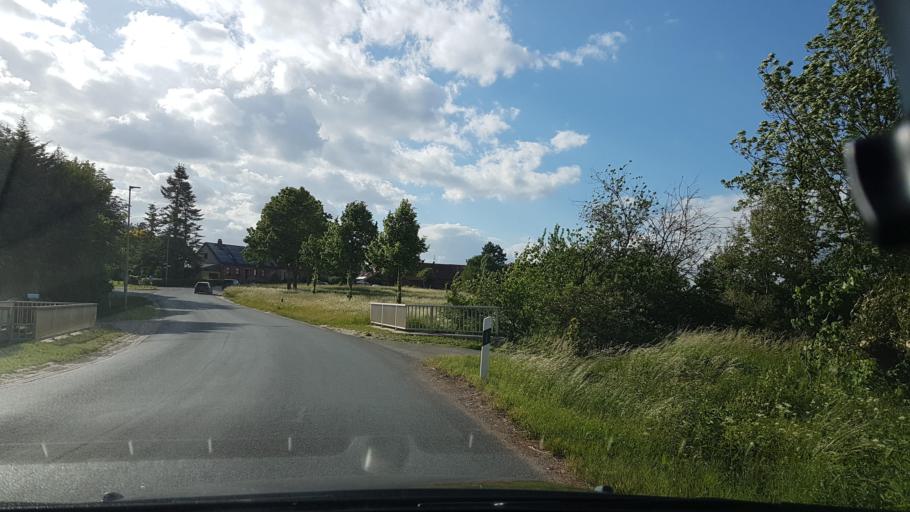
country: DE
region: Lower Saxony
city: Elze
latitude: 52.1429
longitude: 9.6676
